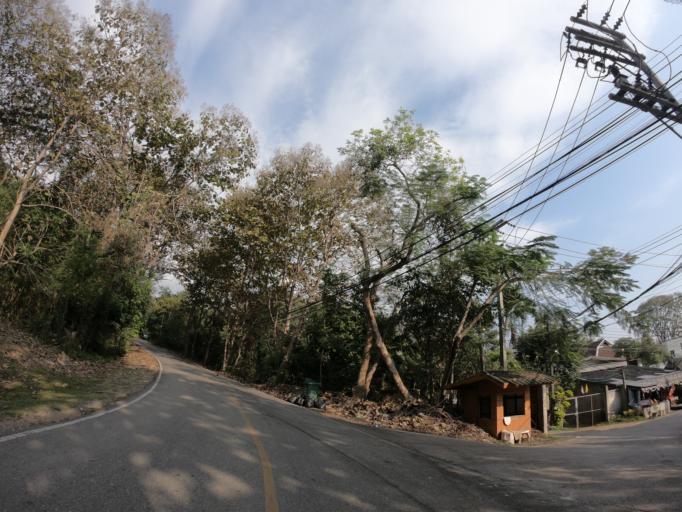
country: TH
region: Chiang Mai
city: Chiang Mai
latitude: 18.7929
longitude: 98.9477
